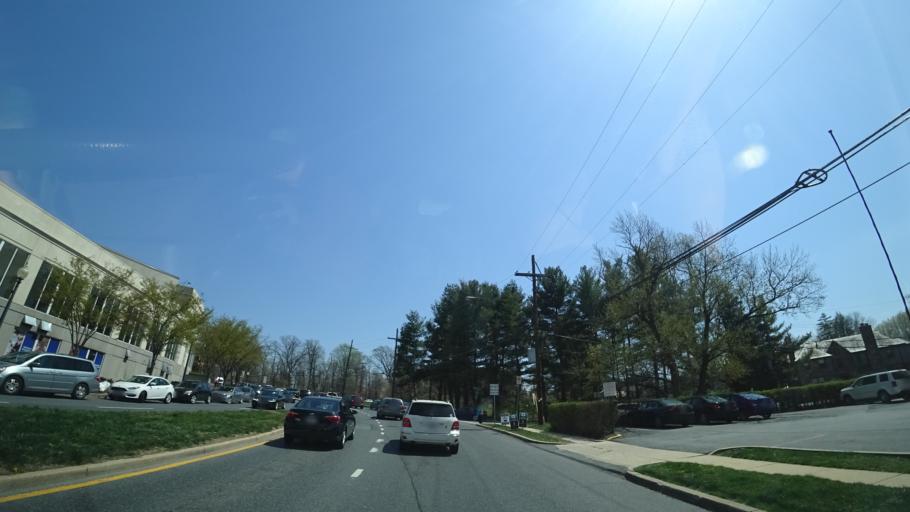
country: US
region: Maryland
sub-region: Montgomery County
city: Bethesda
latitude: 38.9775
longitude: -77.0920
